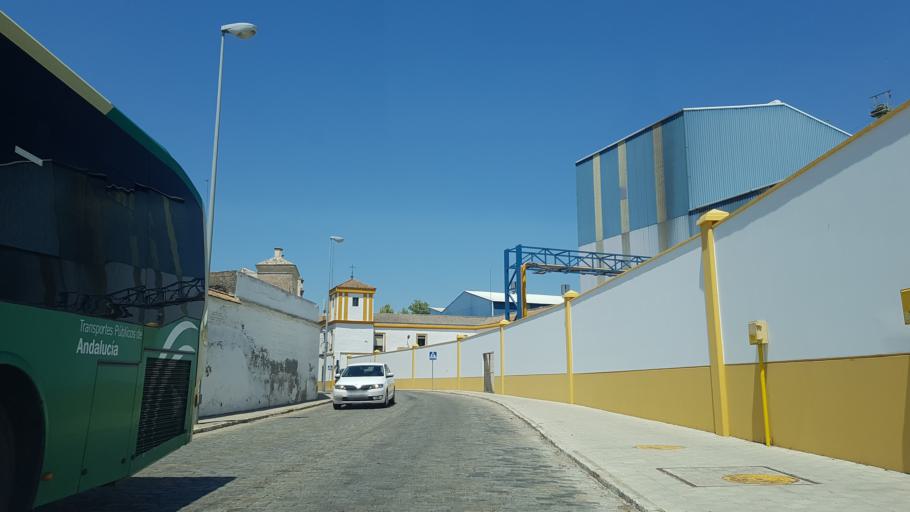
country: ES
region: Andalusia
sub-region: Provincia de Sevilla
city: San Juan de Aznalfarache
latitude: 37.3603
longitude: -6.0258
